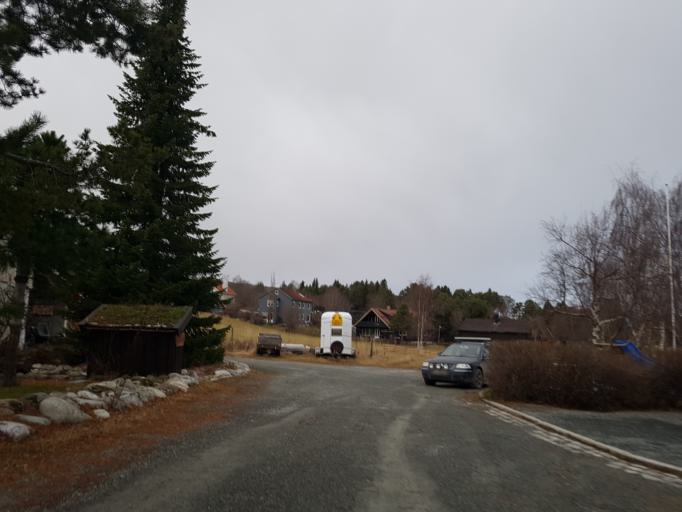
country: NO
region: Sor-Trondelag
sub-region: Trondheim
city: Trondheim
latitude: 63.4132
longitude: 10.3464
